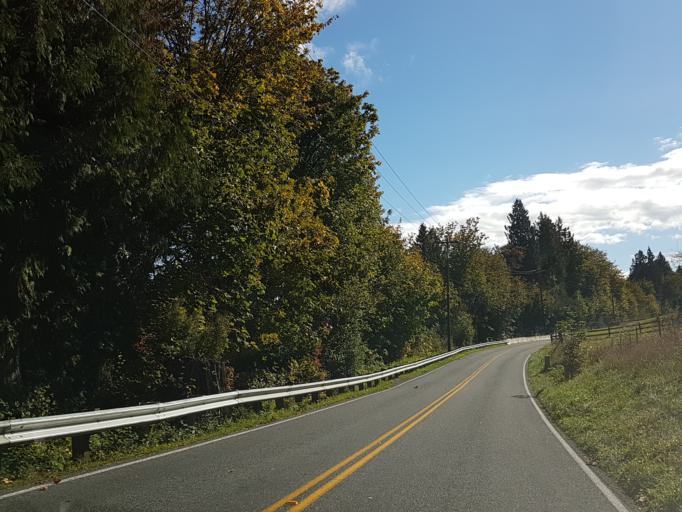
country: US
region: Washington
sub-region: Snohomish County
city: Cathcart
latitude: 47.8392
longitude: -122.0749
